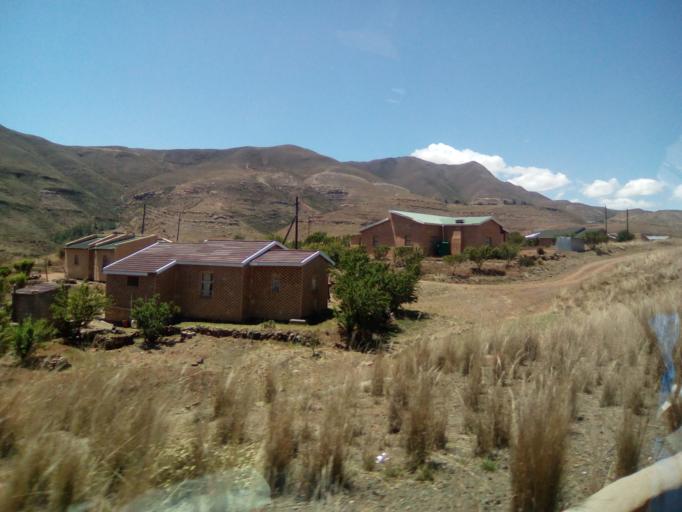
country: LS
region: Qacha's Nek
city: Qacha's Nek
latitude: -30.0891
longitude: 28.6401
